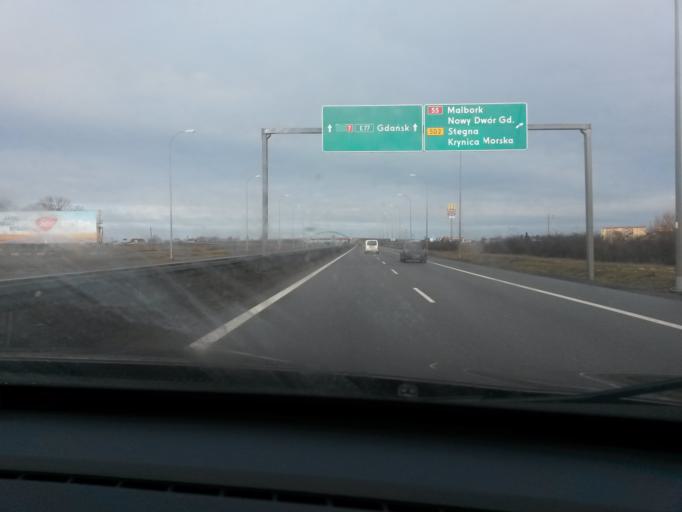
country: PL
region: Pomeranian Voivodeship
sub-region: Powiat nowodworski
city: Nowy Dwor Gdanski
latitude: 54.2076
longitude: 19.1077
